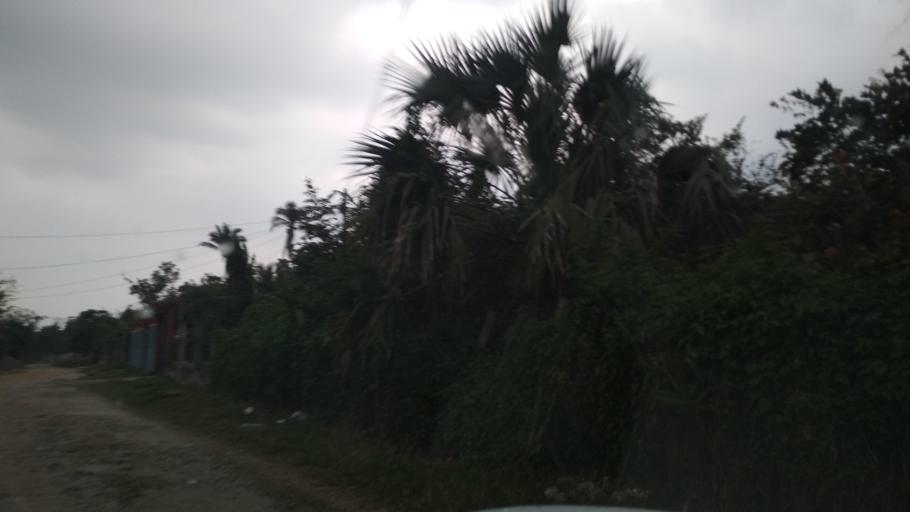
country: MM
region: Shan
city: Taunggyi
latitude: 20.3341
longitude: 97.3099
